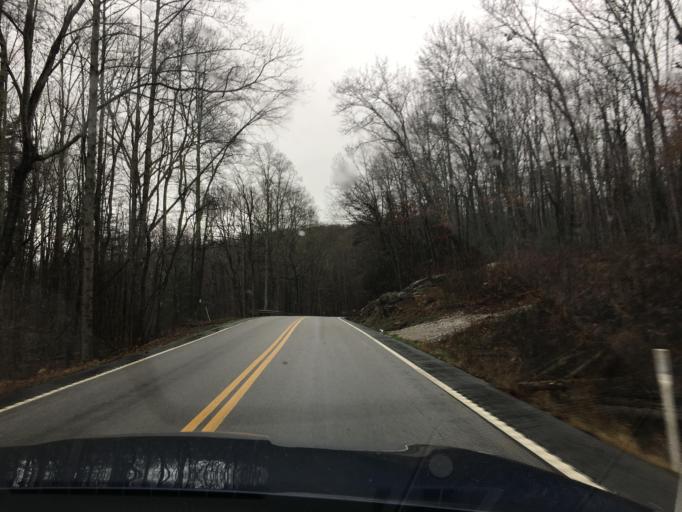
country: US
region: Tennessee
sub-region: Rhea County
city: Spring City
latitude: 35.8270
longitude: -84.9023
